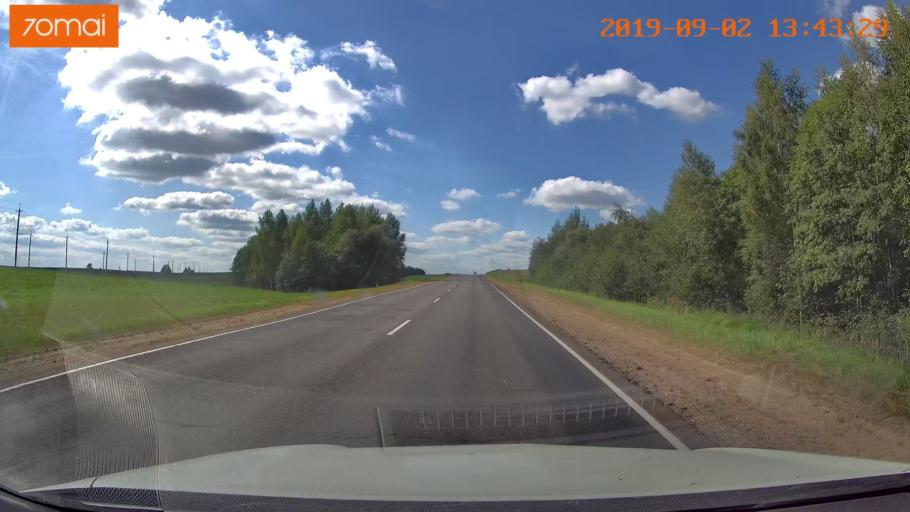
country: BY
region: Mogilev
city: Cherykaw
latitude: 53.5933
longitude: 31.3830
